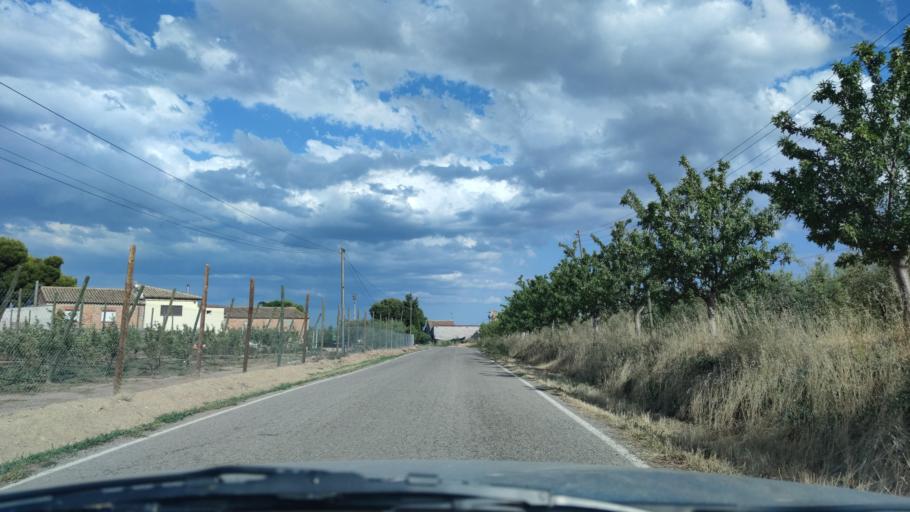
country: ES
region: Catalonia
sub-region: Provincia de Lleida
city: Alpicat
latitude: 41.6308
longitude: 0.5630
